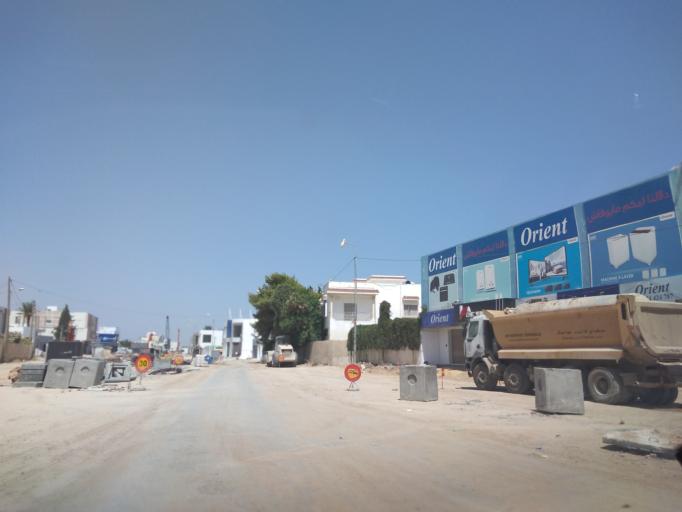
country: TN
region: Safaqis
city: Sfax
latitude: 34.7497
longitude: 10.7290
